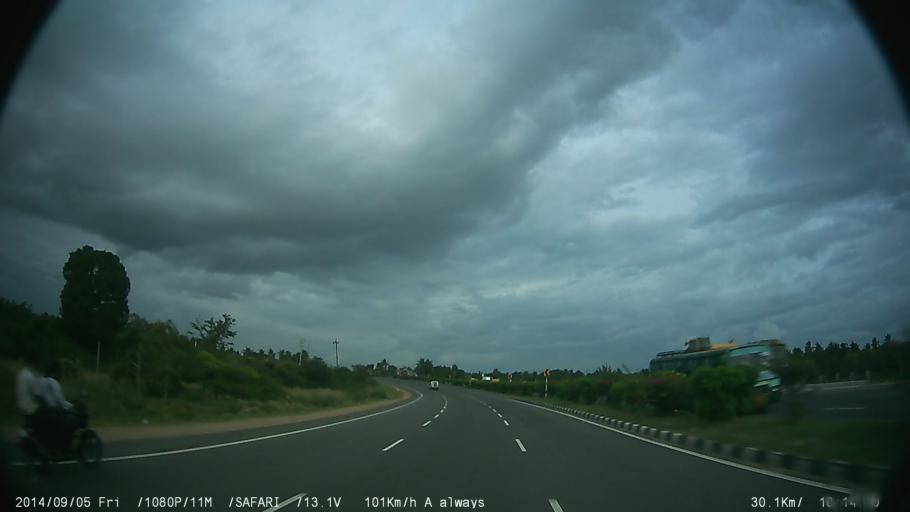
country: IN
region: Tamil Nadu
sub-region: Krishnagiri
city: Kelamangalam
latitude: 12.6810
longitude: 77.9462
